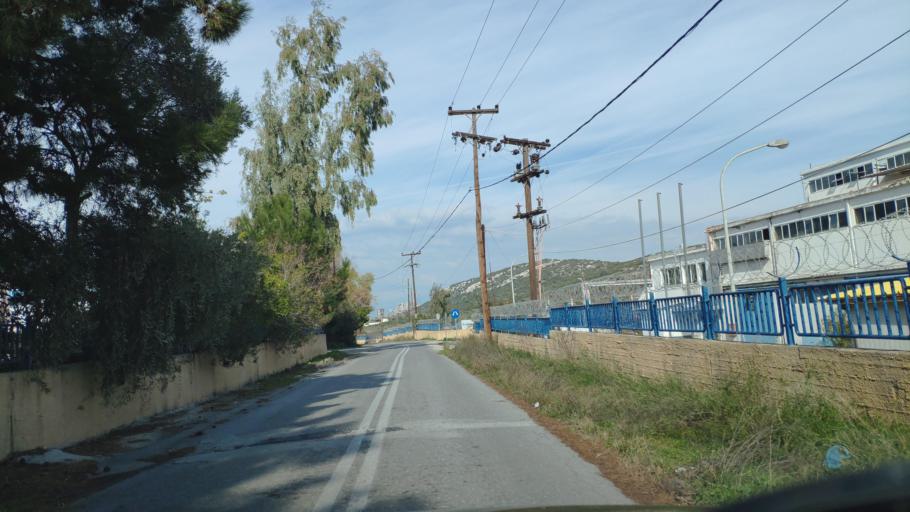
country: GR
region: Central Greece
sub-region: Nomos Evvoias
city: Vathi
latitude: 38.4184
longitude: 23.5914
